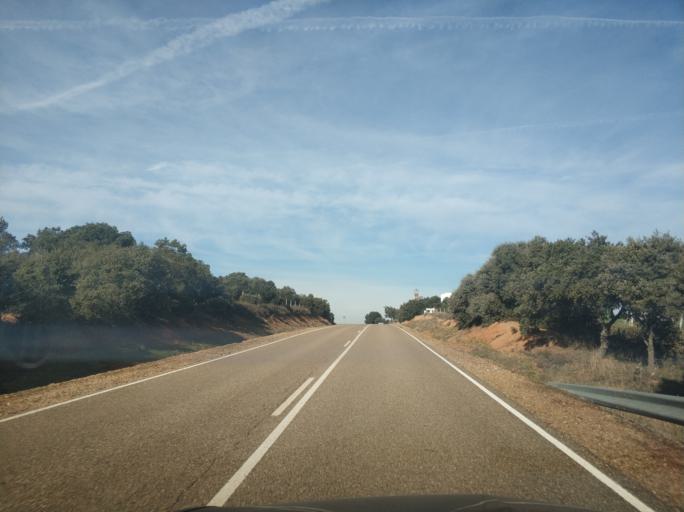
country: ES
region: Castille and Leon
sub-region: Provincia de Salamanca
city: Zarapicos
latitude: 41.0065
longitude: -5.8366
